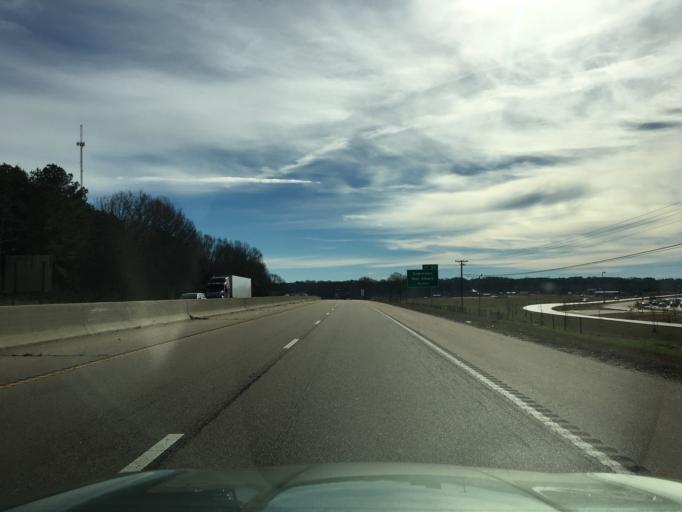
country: US
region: Mississippi
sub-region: Union County
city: New Albany
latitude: 34.4923
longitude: -89.0284
